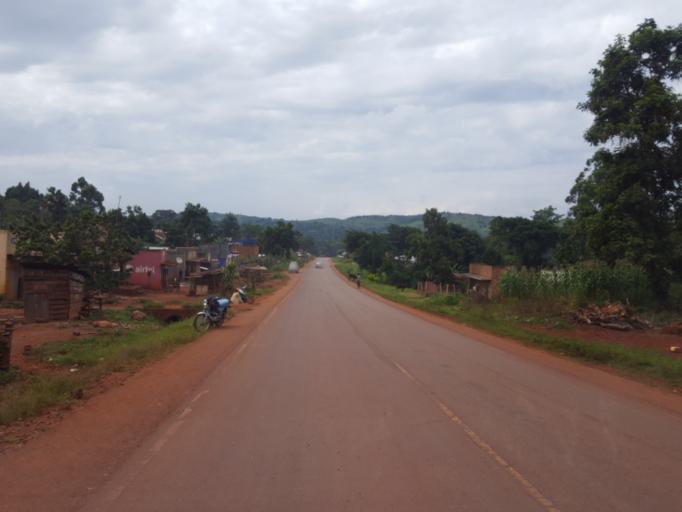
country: UG
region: Central Region
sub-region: Mityana District
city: Mityana
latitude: 0.6347
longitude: 32.1092
